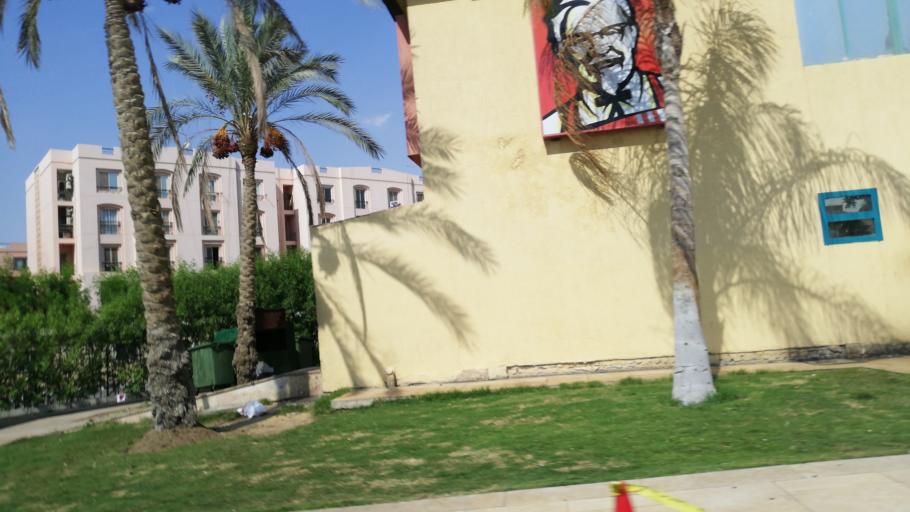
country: EG
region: Muhafazat al Qalyubiyah
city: Al Khankah
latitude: 30.0590
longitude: 31.4881
